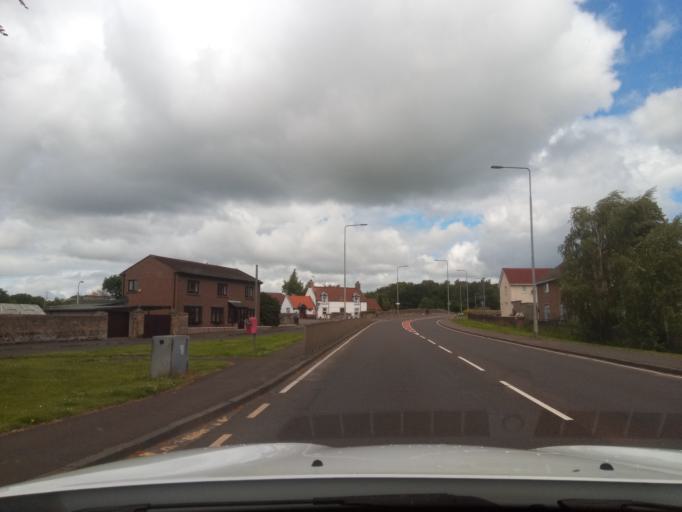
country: GB
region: Scotland
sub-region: Fife
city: Kincardine
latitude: 56.0736
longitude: -3.7205
